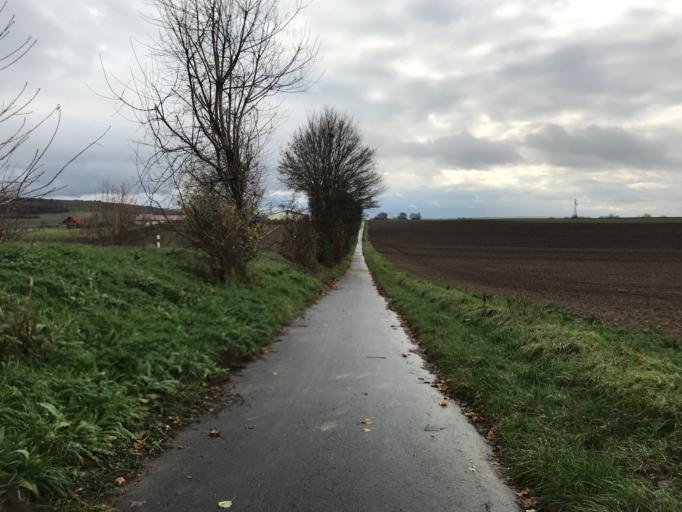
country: DE
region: Rheinland-Pfalz
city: Klein-Winternheim
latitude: 49.9333
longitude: 8.2086
